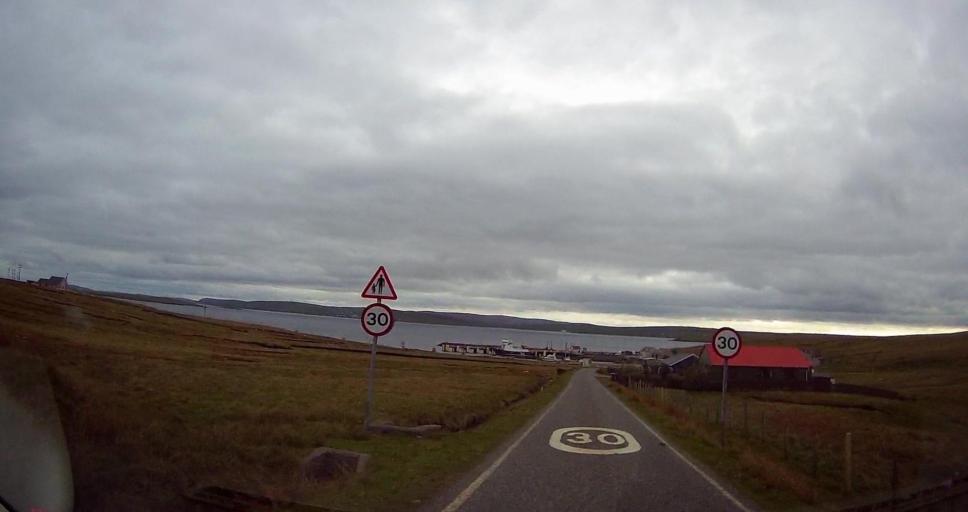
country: GB
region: Scotland
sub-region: Shetland Islands
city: Shetland
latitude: 60.4996
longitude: -1.1535
